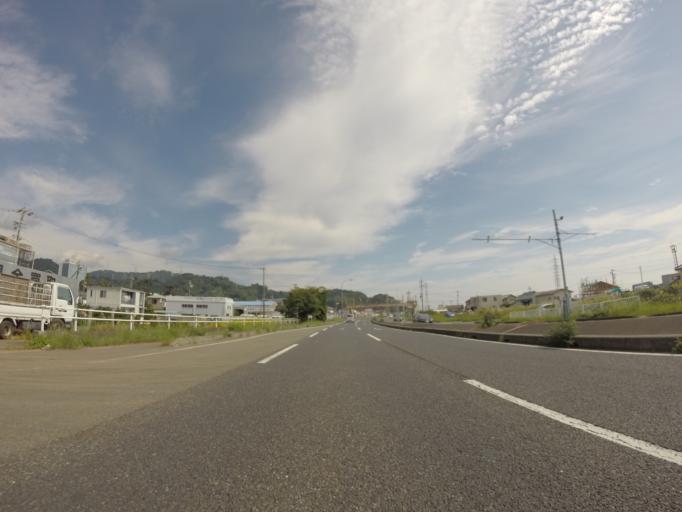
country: JP
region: Shizuoka
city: Shizuoka-shi
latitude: 35.0443
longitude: 138.4902
